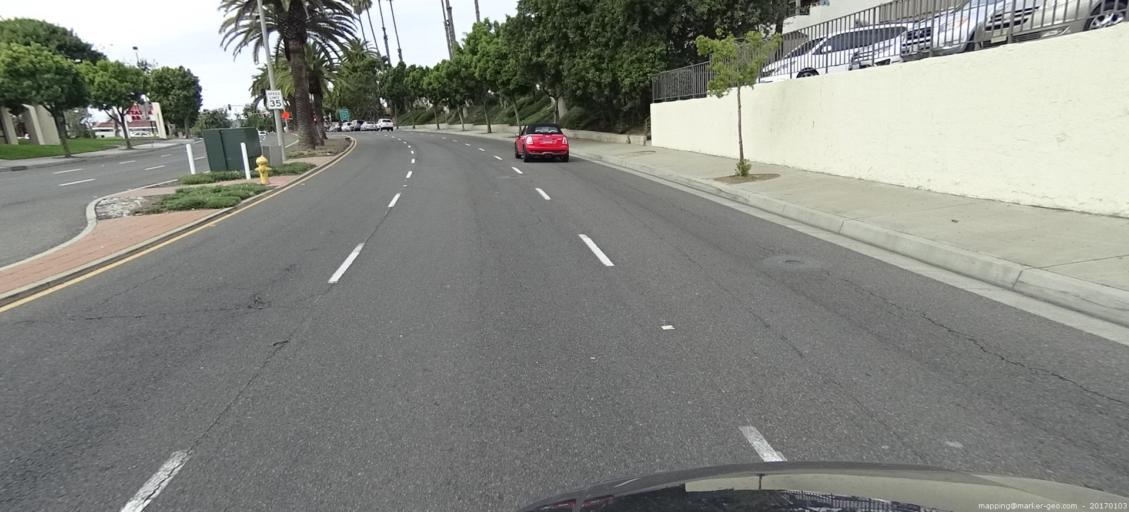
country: US
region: California
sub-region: Orange County
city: San Juan Capistrano
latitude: 33.4597
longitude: -117.6519
